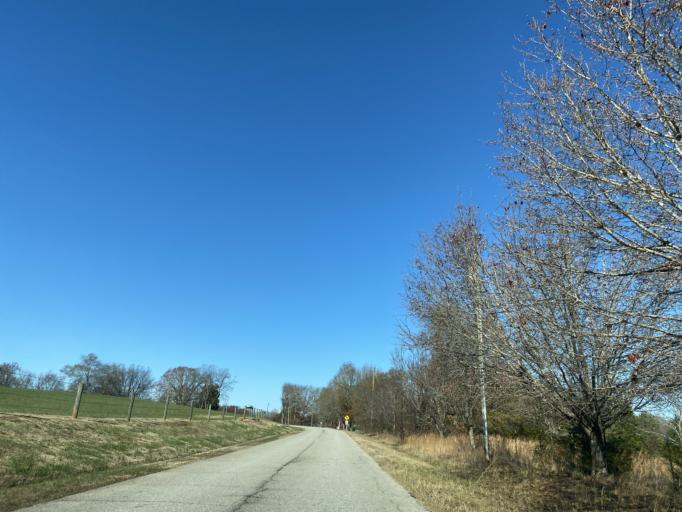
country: US
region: South Carolina
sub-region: Spartanburg County
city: Mayo
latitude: 35.1446
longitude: -81.7850
